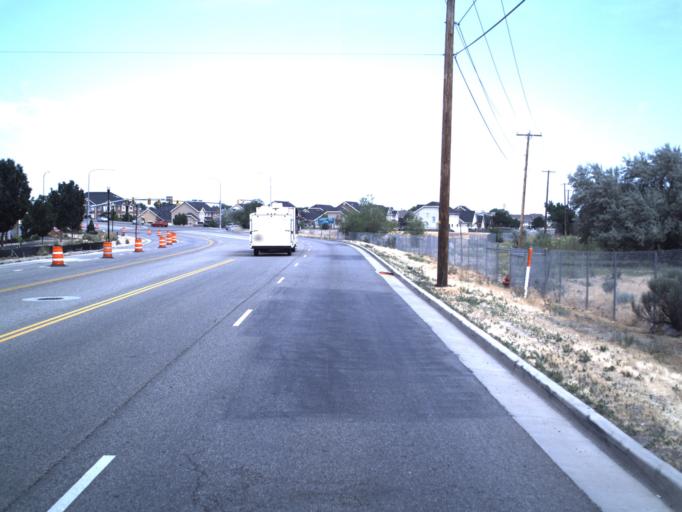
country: US
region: Utah
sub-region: Salt Lake County
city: Draper
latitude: 40.5019
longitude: -111.8851
